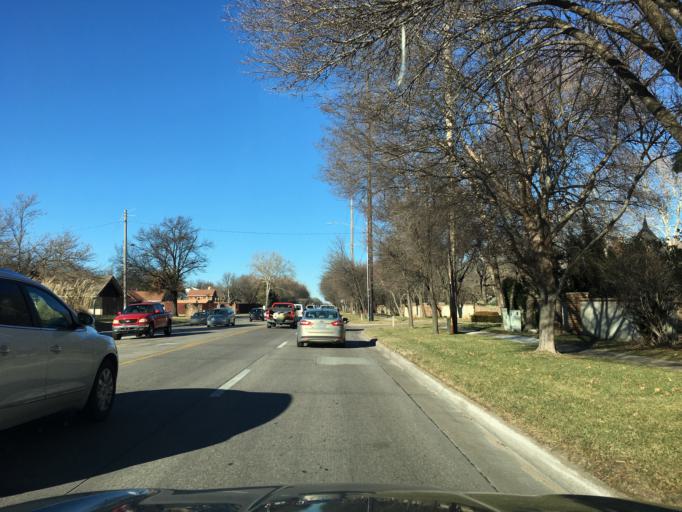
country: US
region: Kansas
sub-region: Sedgwick County
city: Bellaire
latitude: 37.6962
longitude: -97.2445
